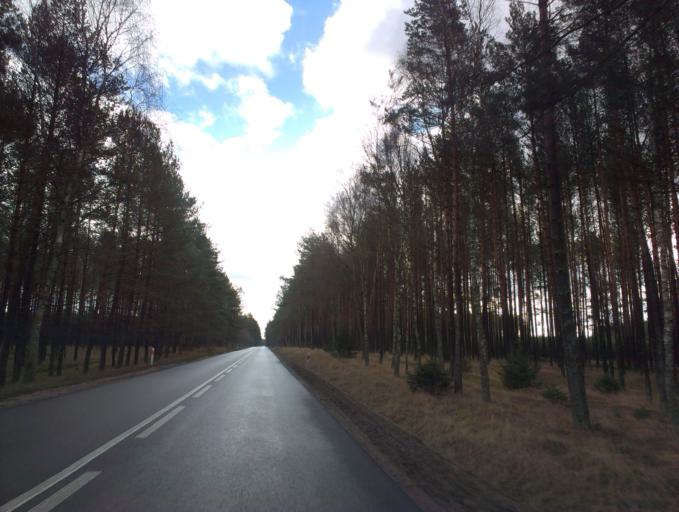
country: PL
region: Pomeranian Voivodeship
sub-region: Powiat czluchowski
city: Czarne
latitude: 53.7005
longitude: 16.8812
